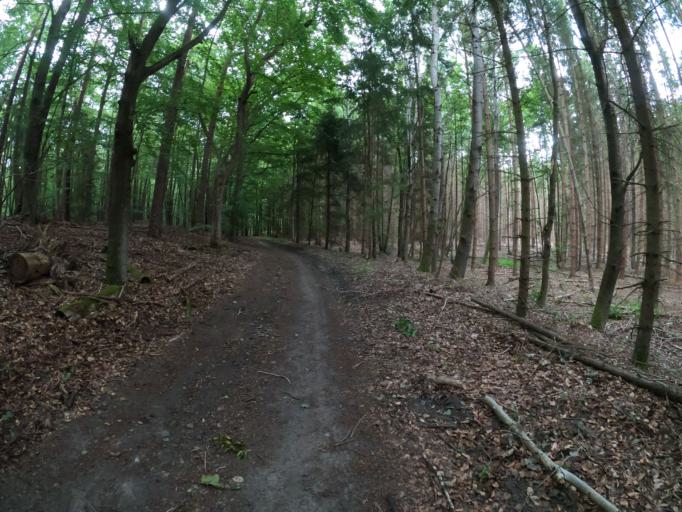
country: DE
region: Brandenburg
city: Angermunde
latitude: 53.0301
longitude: 13.9266
